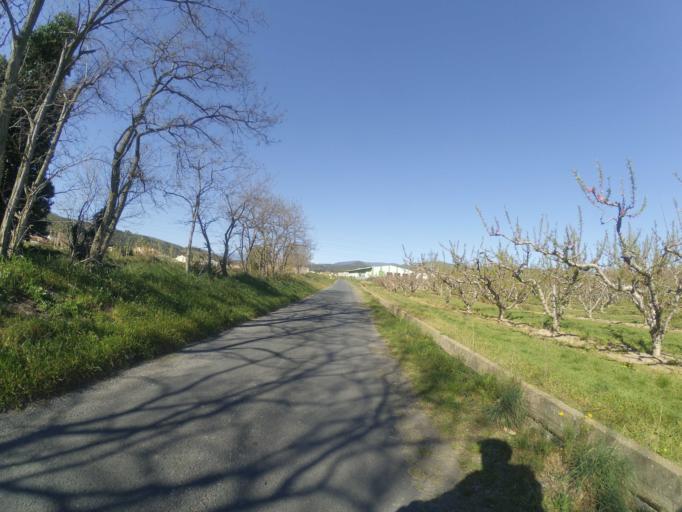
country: FR
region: Languedoc-Roussillon
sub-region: Departement des Pyrenees-Orientales
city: Ille-sur-Tet
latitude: 42.6532
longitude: 2.5918
